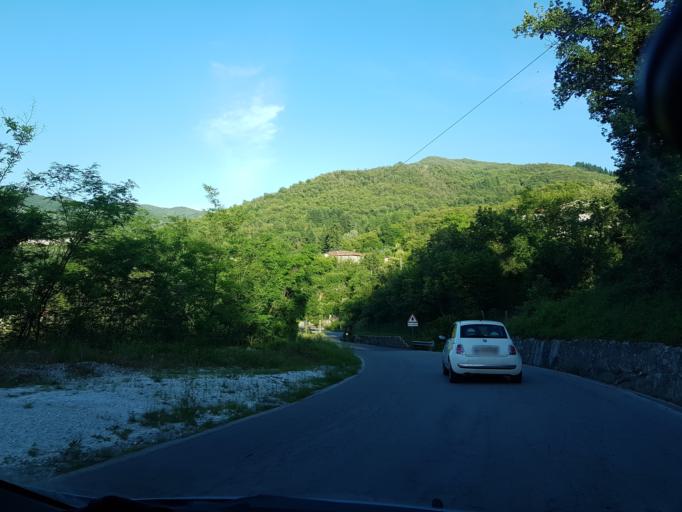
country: IT
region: Tuscany
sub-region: Provincia di Massa-Carrara
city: Casola in Lunigiana
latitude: 44.1919
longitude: 10.1955
